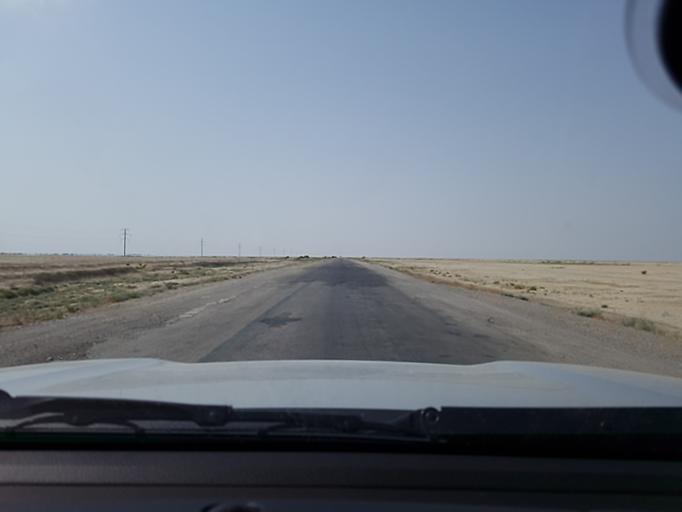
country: TM
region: Balkan
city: Gumdag
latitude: 38.8893
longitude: 54.5930
